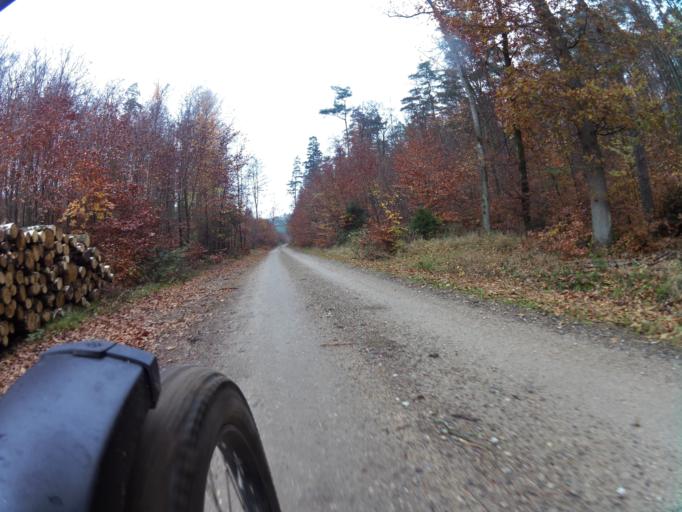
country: PL
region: Pomeranian Voivodeship
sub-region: Powiat wejherowski
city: Orle
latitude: 54.7047
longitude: 18.1456
